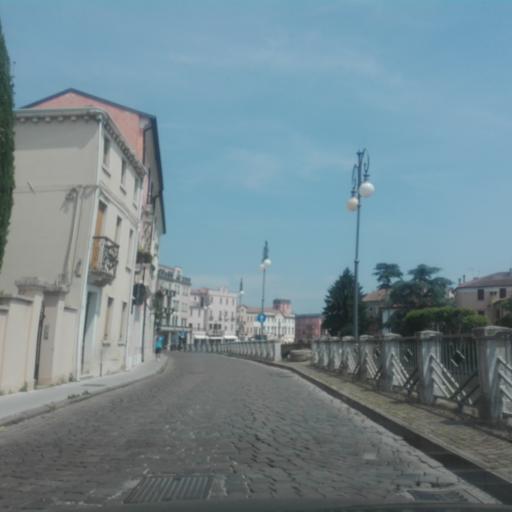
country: IT
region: Veneto
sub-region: Provincia di Rovigo
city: Adria
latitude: 45.0548
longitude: 12.0547
